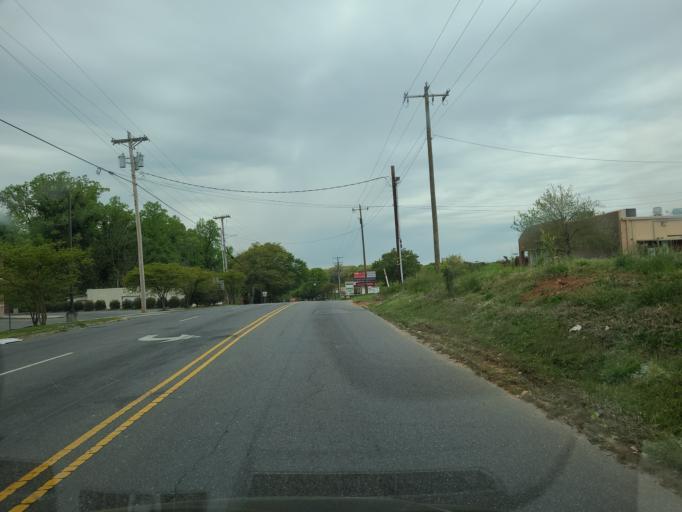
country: US
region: North Carolina
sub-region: Cleveland County
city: Shelby
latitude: 35.2952
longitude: -81.5122
